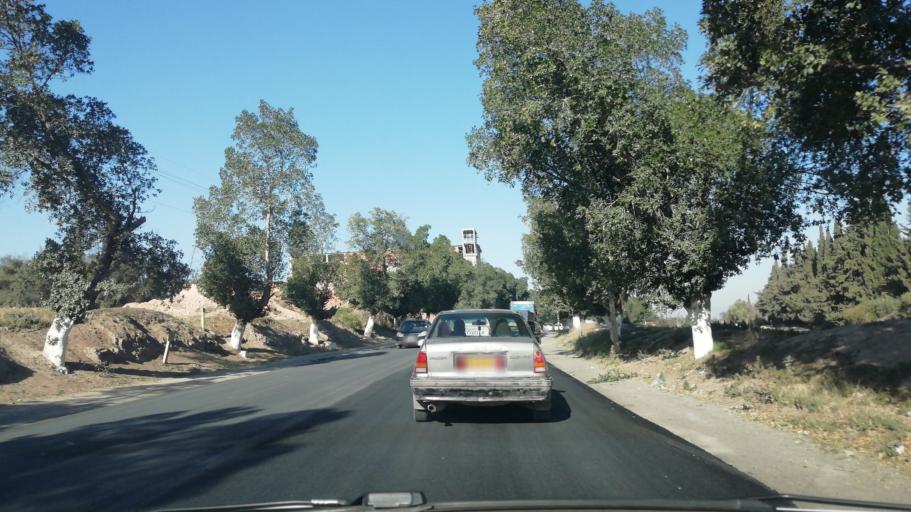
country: DZ
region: Mascara
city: Mascara
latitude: 35.5828
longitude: 0.0454
